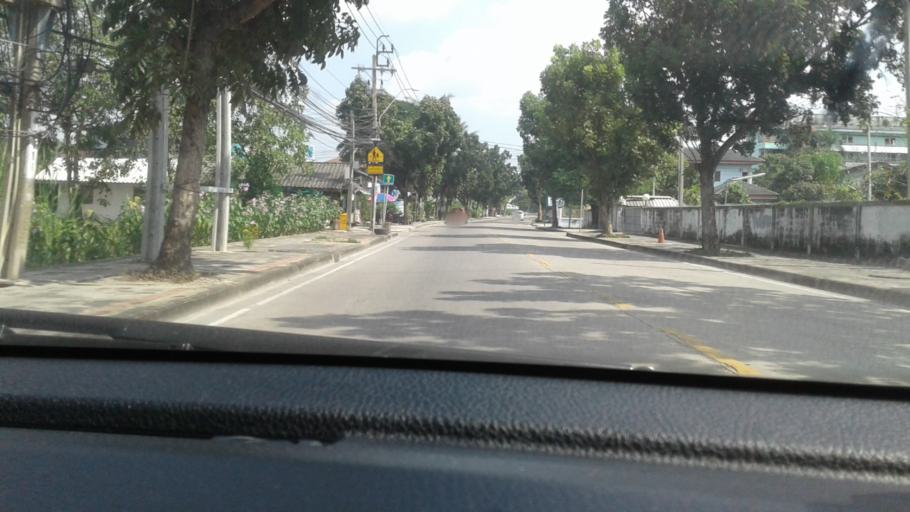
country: TH
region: Bangkok
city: Taling Chan
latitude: 13.7899
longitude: 100.4073
